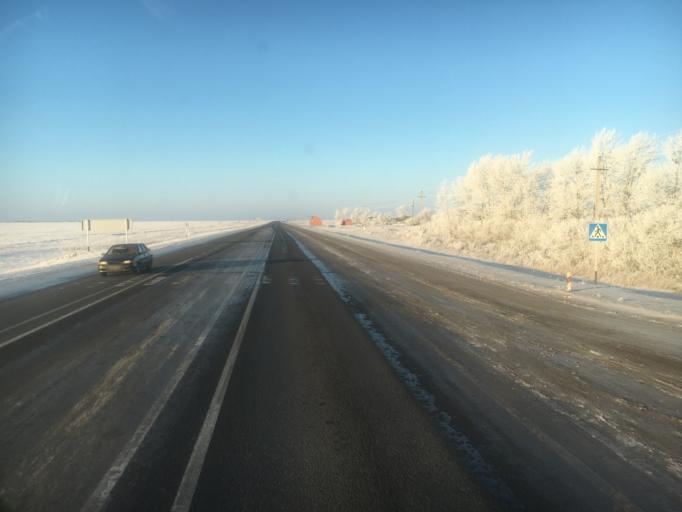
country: KZ
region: Soltustik Qazaqstan
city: Taiynsha
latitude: 53.7503
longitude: 69.3625
